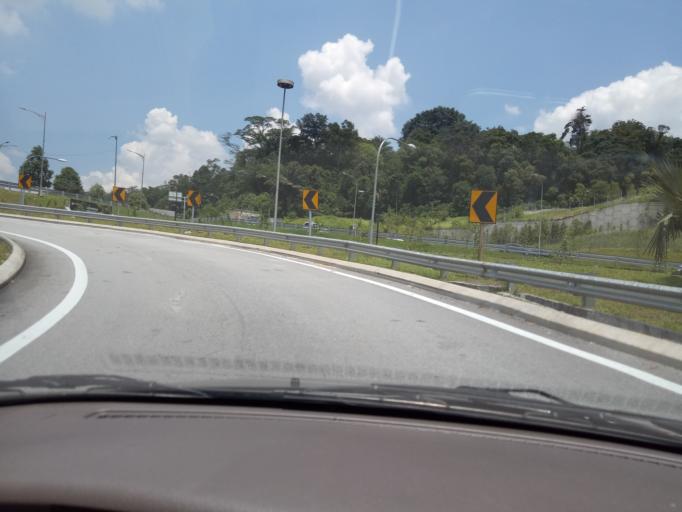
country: MY
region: Kuala Lumpur
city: Kuala Lumpur
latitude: 3.1462
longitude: 101.6785
